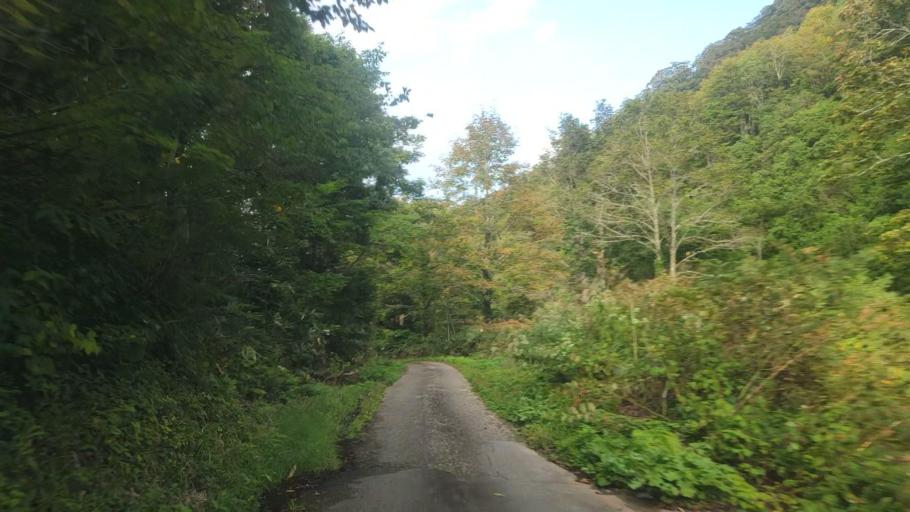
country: JP
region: Toyama
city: Yatsuomachi-higashikumisaka
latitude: 36.3617
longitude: 137.0703
